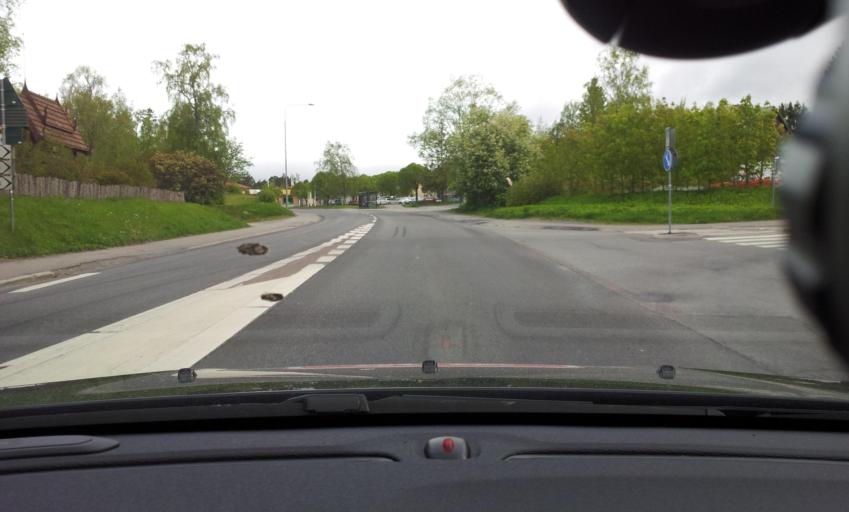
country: SE
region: Jaemtland
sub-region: OEstersunds Kommun
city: Brunflo
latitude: 63.0791
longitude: 14.8273
